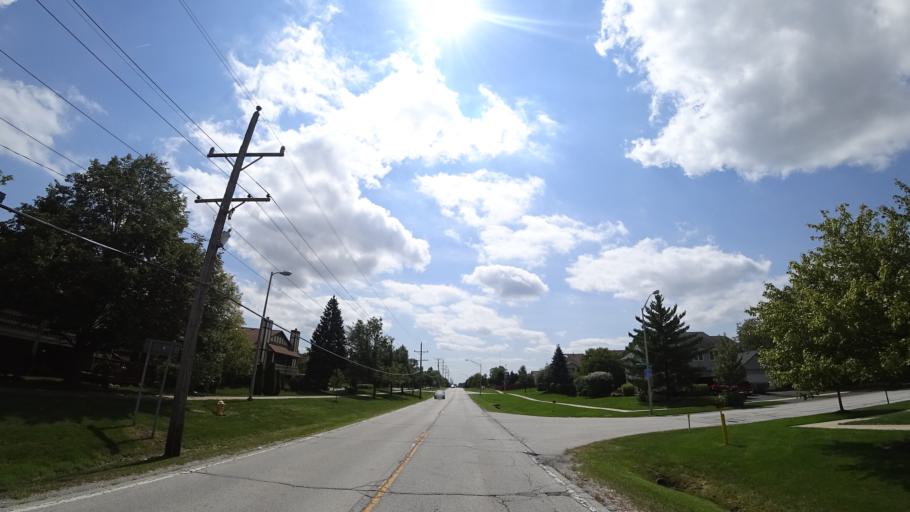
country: US
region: Illinois
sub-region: Cook County
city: Orland Hills
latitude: 41.5712
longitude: -87.8468
